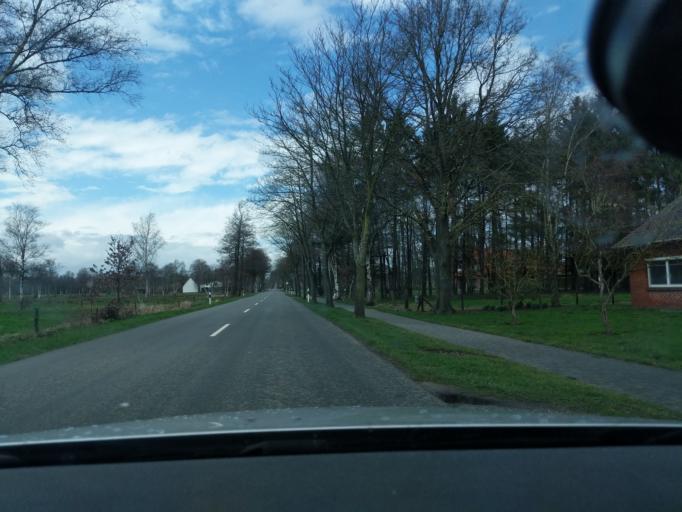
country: DE
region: Lower Saxony
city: Engelschoff
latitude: 53.6737
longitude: 9.3655
